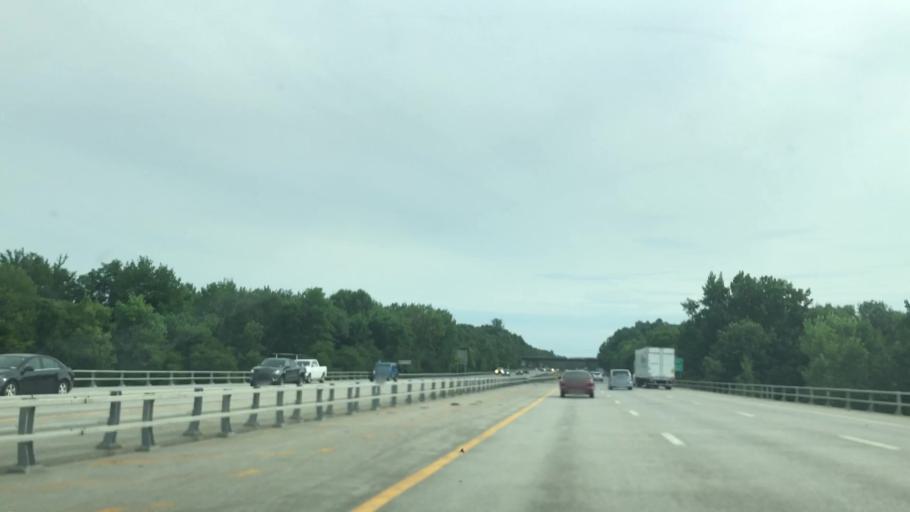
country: US
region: New York
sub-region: Warren County
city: West Glens Falls
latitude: 43.2636
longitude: -73.6765
